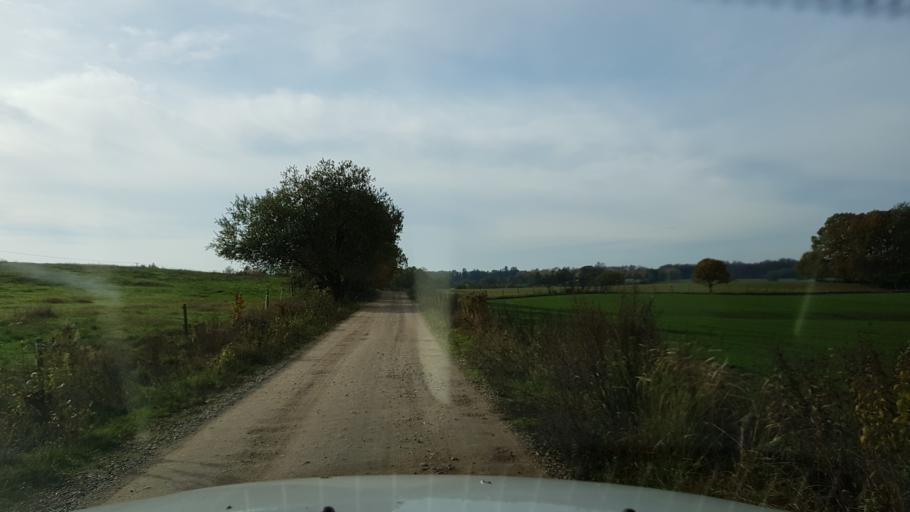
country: PL
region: West Pomeranian Voivodeship
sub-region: Powiat swidwinski
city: Polczyn-Zdroj
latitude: 53.7325
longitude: 16.0316
